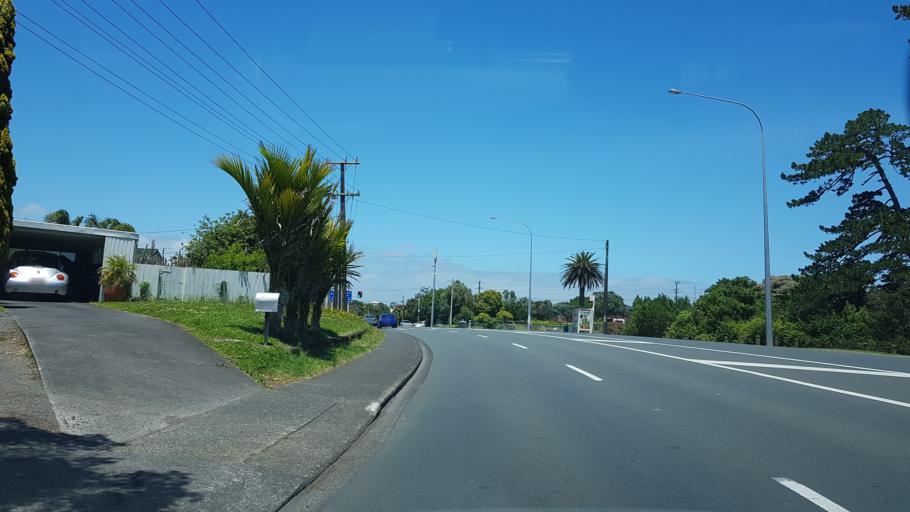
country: NZ
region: Auckland
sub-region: Auckland
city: North Shore
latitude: -36.7977
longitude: 174.7234
